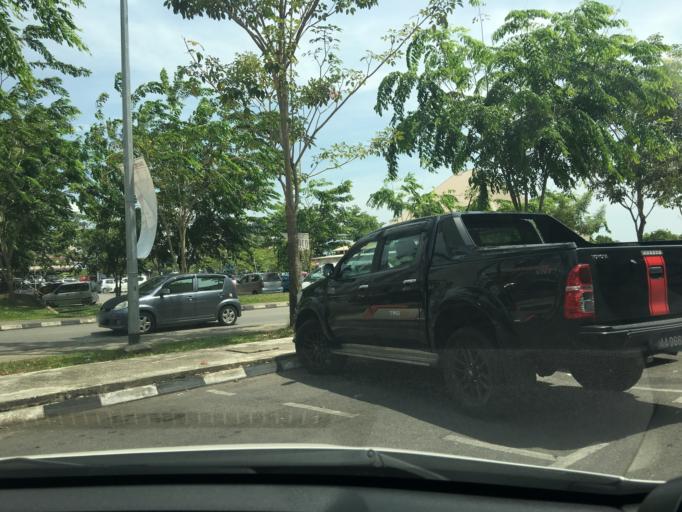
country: MY
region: Sarawak
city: Kuching
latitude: 1.5076
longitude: 110.3001
